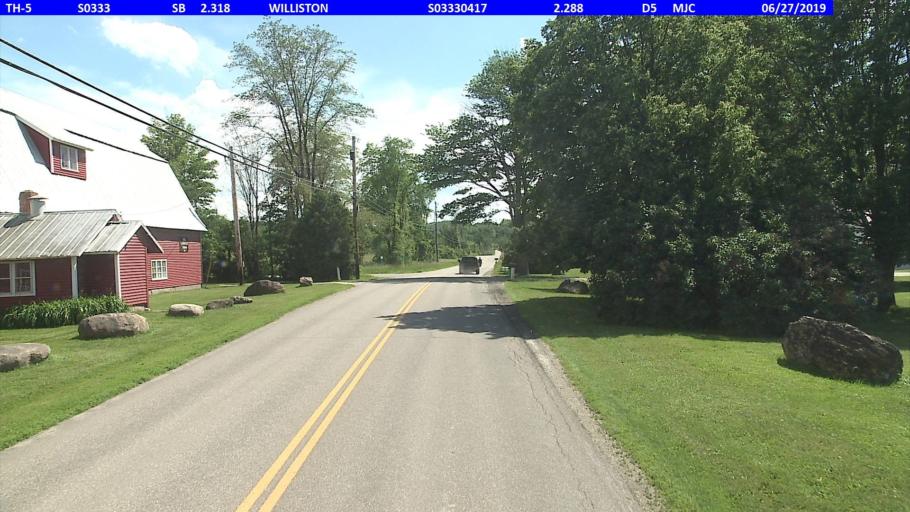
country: US
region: Vermont
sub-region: Chittenden County
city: South Burlington
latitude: 44.4339
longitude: -73.1317
